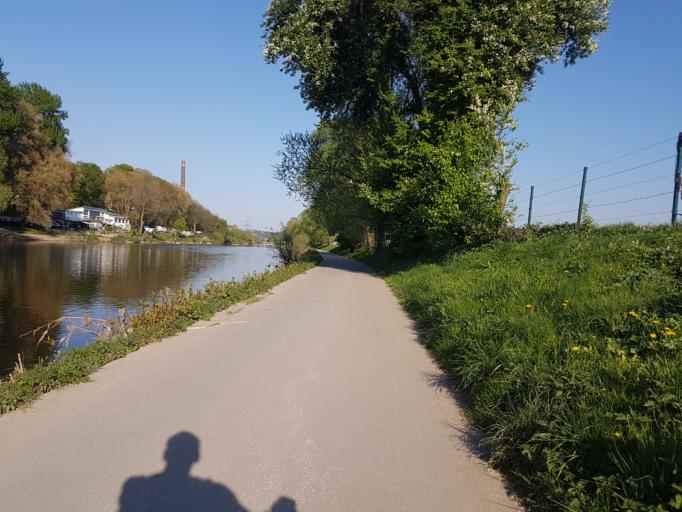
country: DE
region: North Rhine-Westphalia
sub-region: Regierungsbezirk Munster
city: Gelsenkirchen
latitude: 51.4283
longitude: 7.1010
